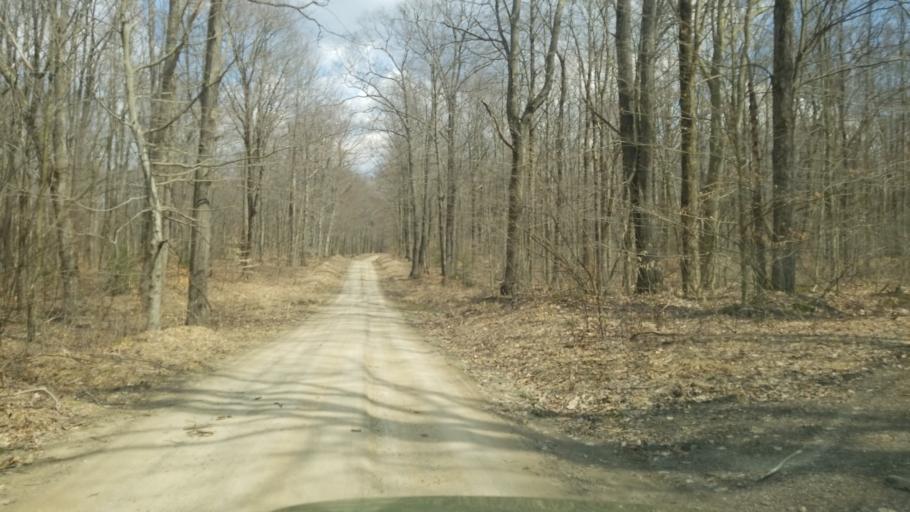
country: US
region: Pennsylvania
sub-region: Clearfield County
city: Clearfield
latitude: 41.1611
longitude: -78.5073
